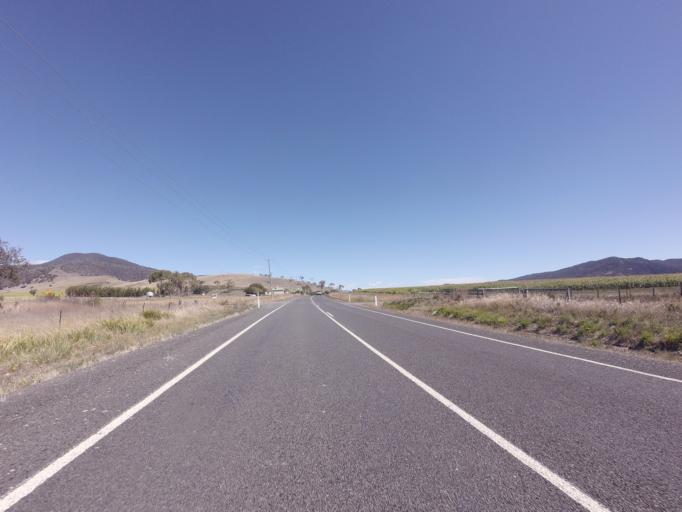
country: AU
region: Tasmania
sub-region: Break O'Day
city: St Helens
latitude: -41.7174
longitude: 147.8344
